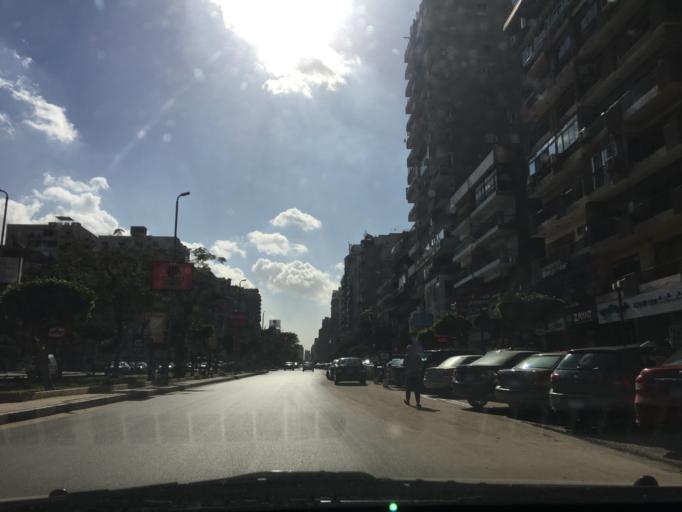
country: EG
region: Muhafazat al Qahirah
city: Cairo
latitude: 30.0613
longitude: 31.3451
